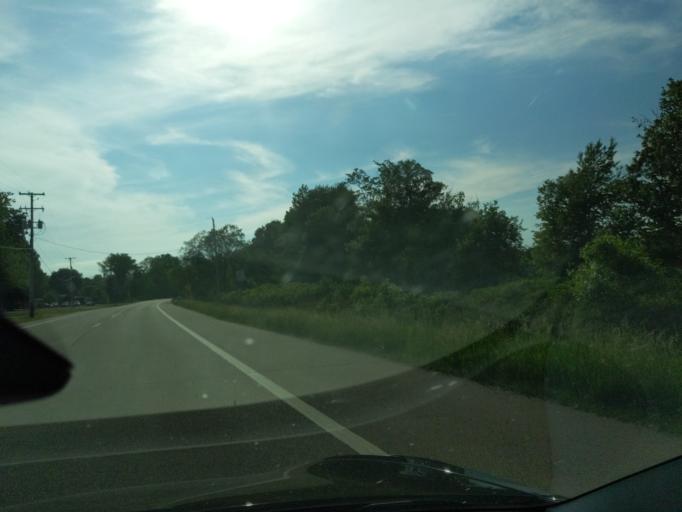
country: US
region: Michigan
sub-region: Barry County
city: Nashville
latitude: 42.5986
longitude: -85.1013
